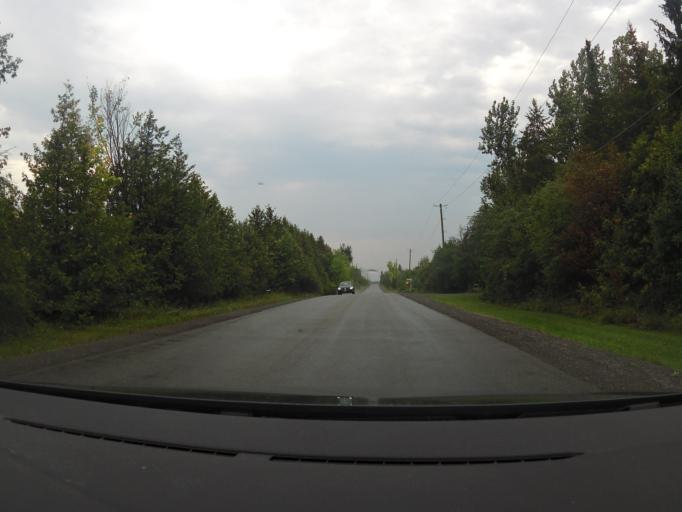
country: CA
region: Ontario
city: Carleton Place
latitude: 45.1998
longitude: -76.0619
